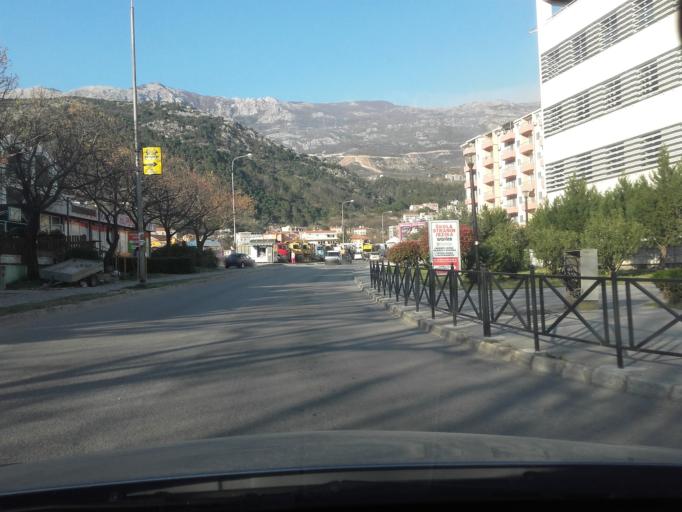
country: ME
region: Budva
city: Budva
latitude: 42.2935
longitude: 18.8389
